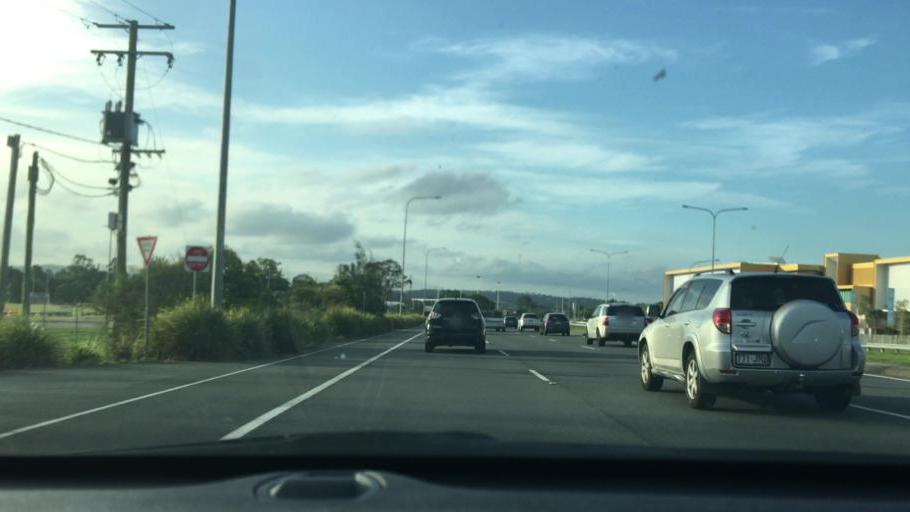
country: AU
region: Queensland
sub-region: Gold Coast
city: Nerang
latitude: -28.0072
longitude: 153.3648
